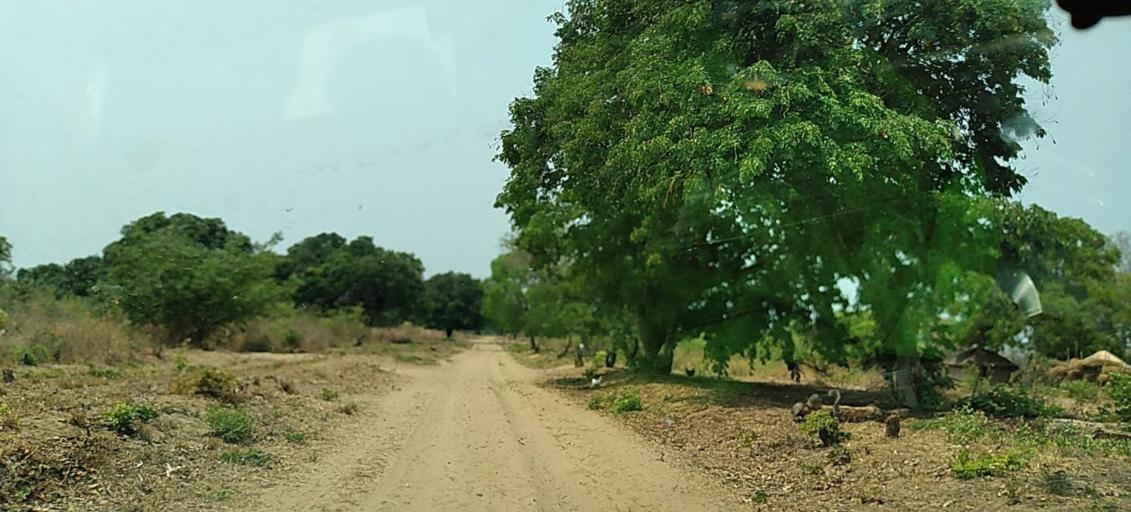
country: ZM
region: Western
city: Lukulu
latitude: -13.9971
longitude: 23.2339
